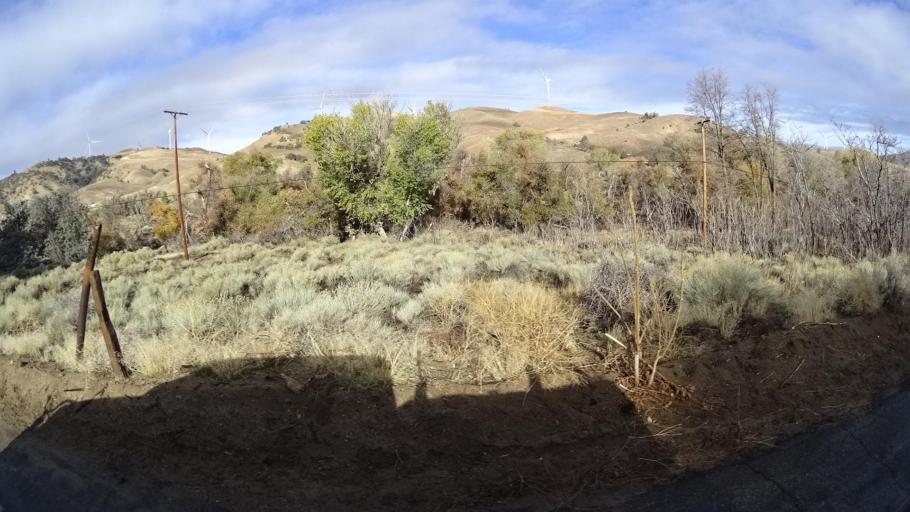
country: US
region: California
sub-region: Kern County
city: Tehachapi
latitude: 35.0798
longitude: -118.3279
